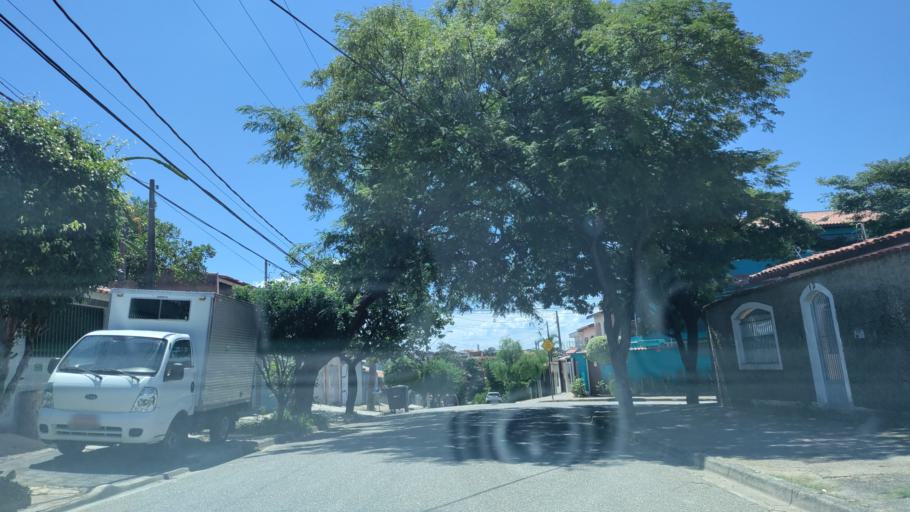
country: BR
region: Sao Paulo
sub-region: Sorocaba
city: Sorocaba
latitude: -23.4606
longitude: -47.4764
